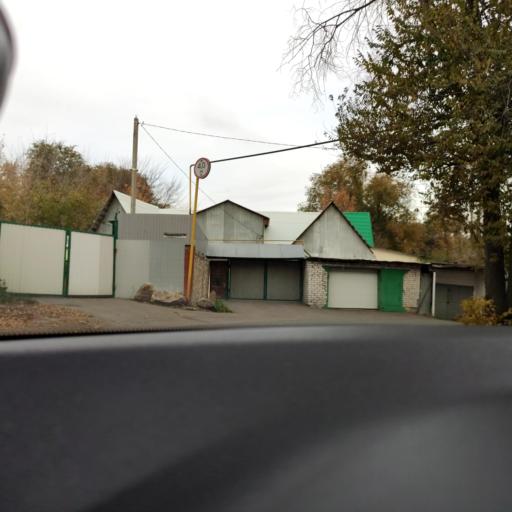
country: RU
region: Samara
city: Samara
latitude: 53.2396
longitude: 50.2571
